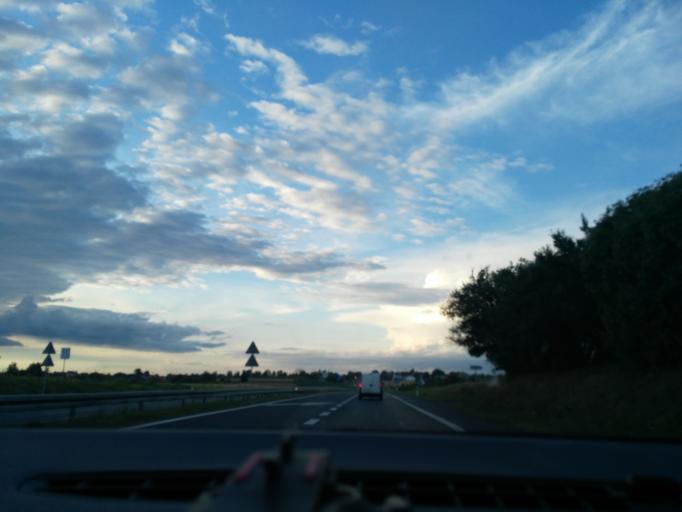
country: PL
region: Lublin Voivodeship
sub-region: Powiat lubelski
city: Niemce
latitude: 51.3390
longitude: 22.6184
